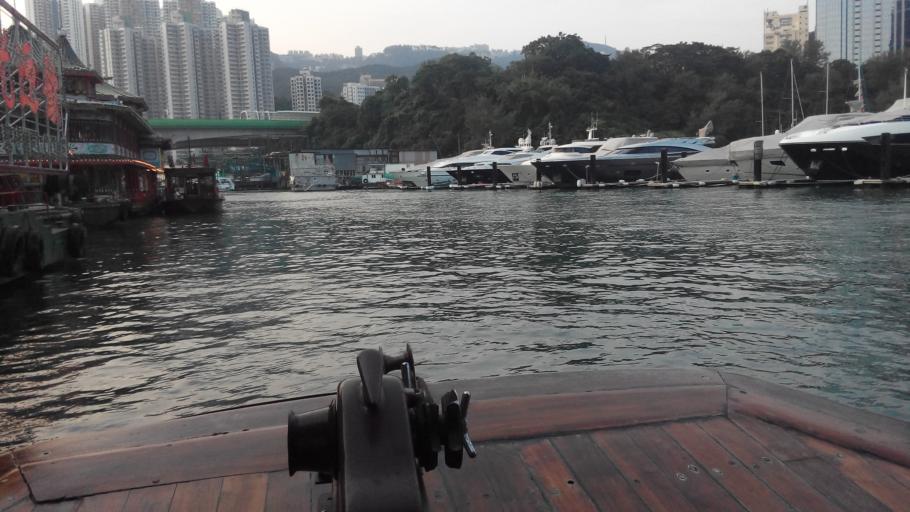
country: HK
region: Wanchai
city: Wan Chai
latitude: 22.2435
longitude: 114.1620
